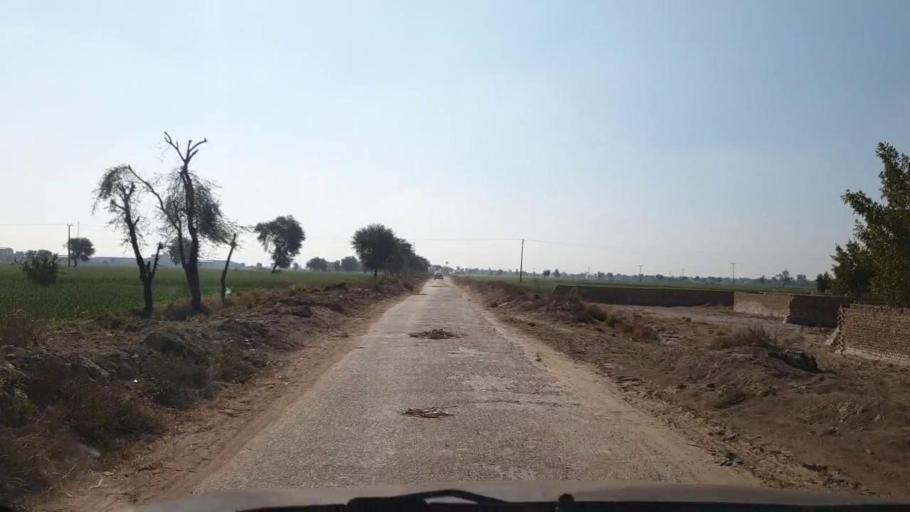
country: PK
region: Sindh
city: Sinjhoro
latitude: 25.9470
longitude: 68.7469
